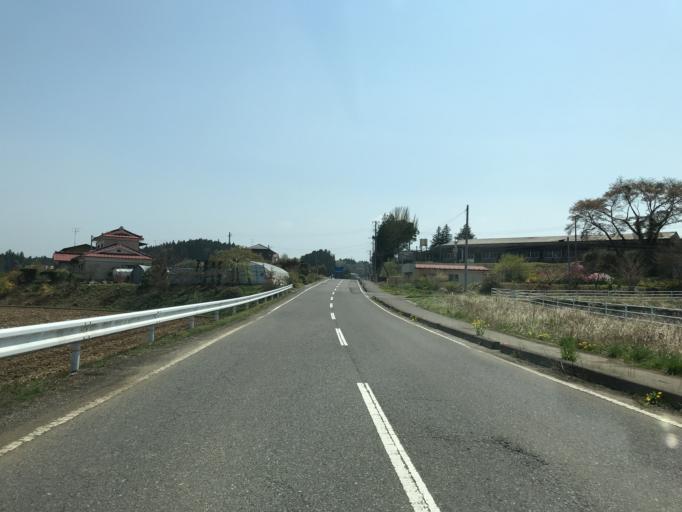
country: JP
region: Fukushima
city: Ishikawa
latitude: 37.1107
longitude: 140.3834
